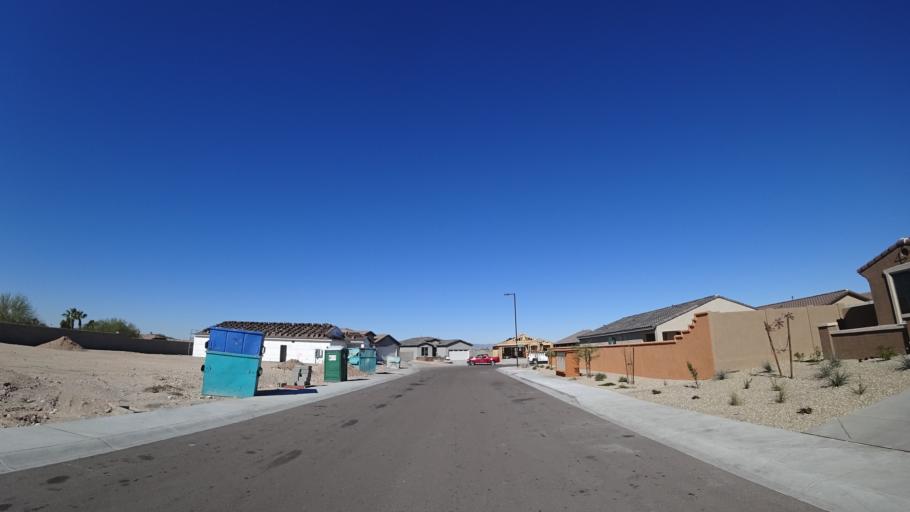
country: US
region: Arizona
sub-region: Maricopa County
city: Goodyear
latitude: 33.3462
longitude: -112.4261
